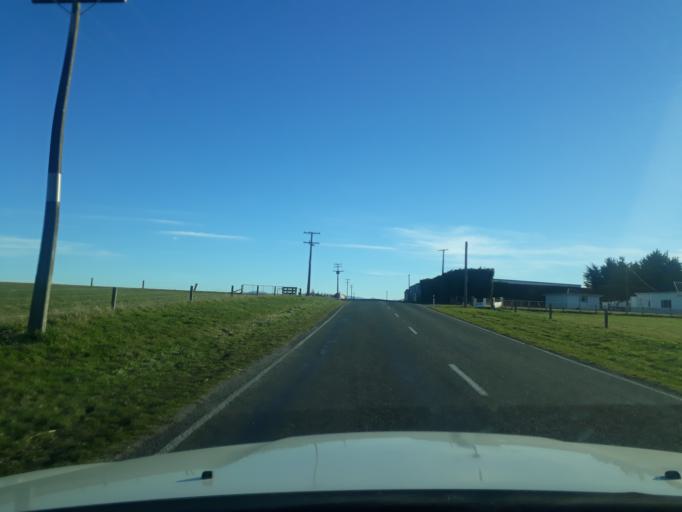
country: NZ
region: Canterbury
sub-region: Timaru District
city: Timaru
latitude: -44.3361
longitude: 171.2229
